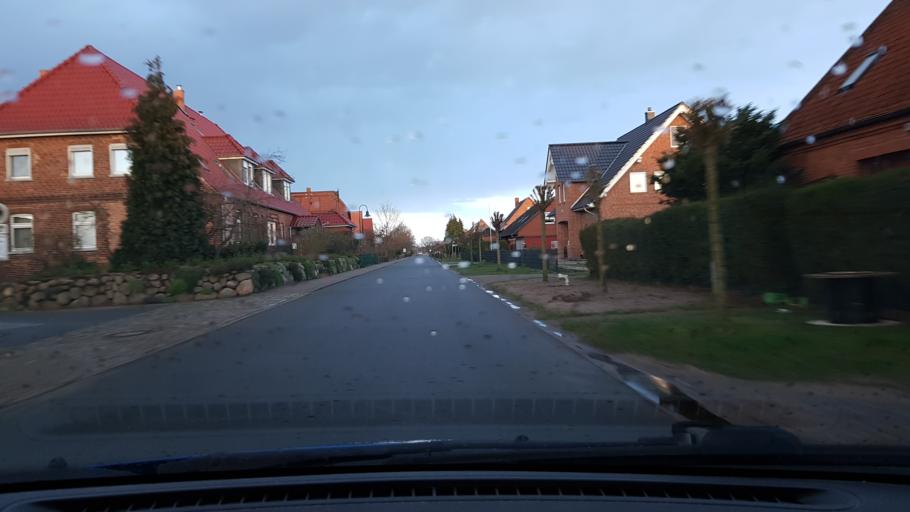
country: DE
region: Lower Saxony
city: Echem
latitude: 53.3366
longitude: 10.5379
